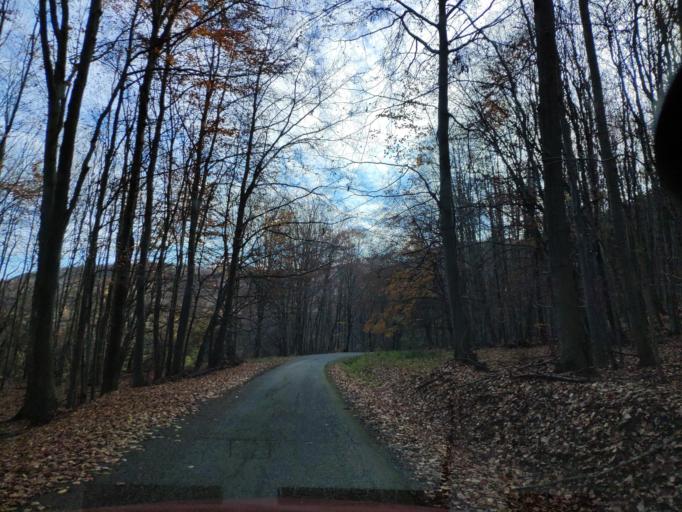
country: HU
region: Borsod-Abauj-Zemplen
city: Gonc
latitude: 48.5937
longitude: 21.4523
